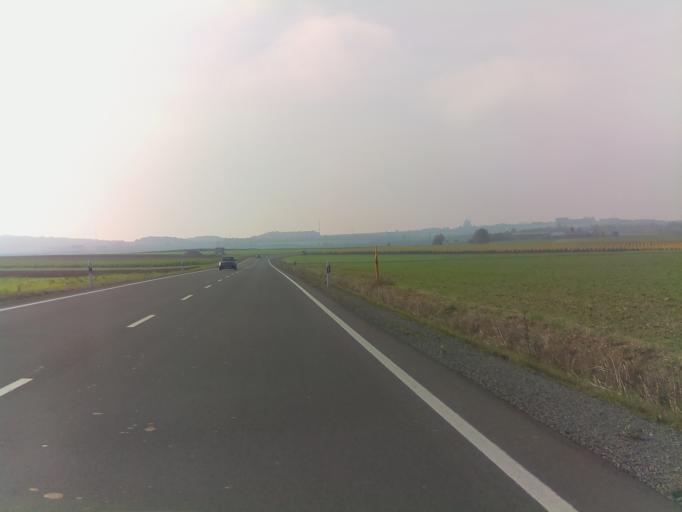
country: DE
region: Bavaria
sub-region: Regierungsbezirk Unterfranken
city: Mainstockheim
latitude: 49.7942
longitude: 10.1244
